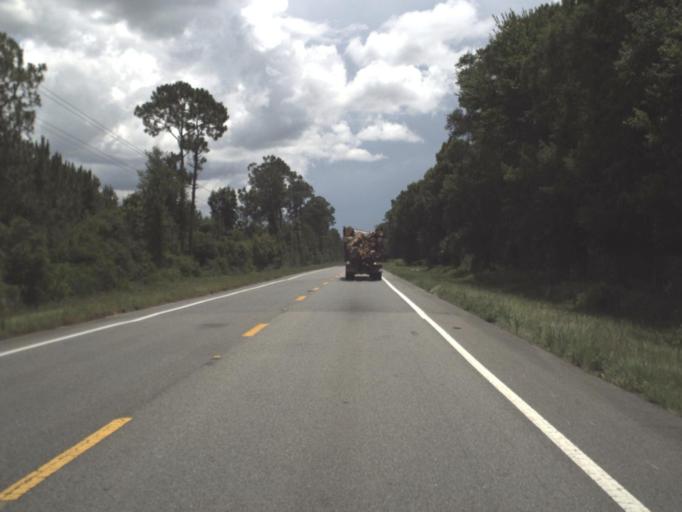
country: US
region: Florida
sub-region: Taylor County
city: Perry
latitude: 30.0917
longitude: -83.6803
